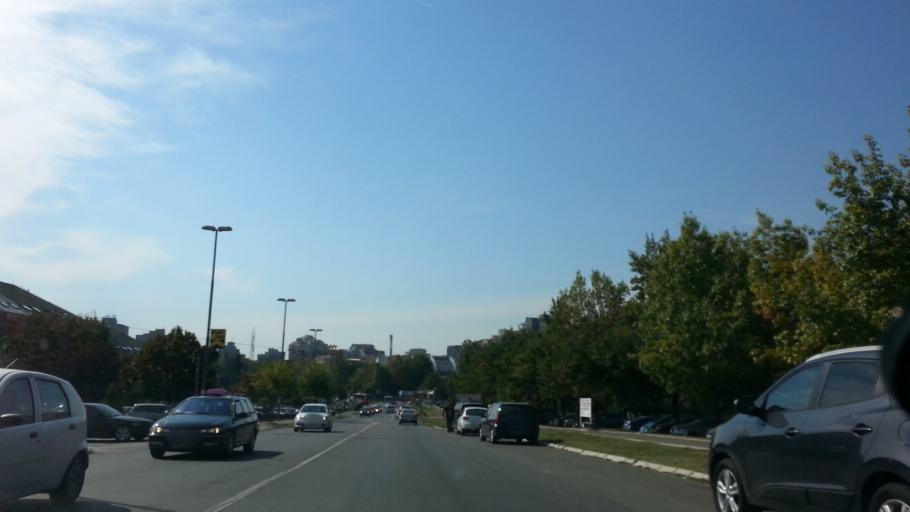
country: RS
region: Central Serbia
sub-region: Belgrade
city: Rakovica
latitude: 44.7453
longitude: 20.4271
